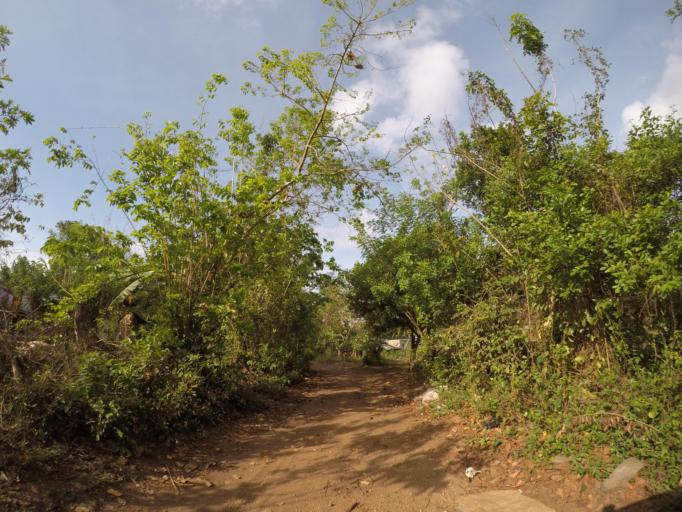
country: TZ
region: Zanzibar Central/South
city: Koani
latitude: -6.2172
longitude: 39.3213
